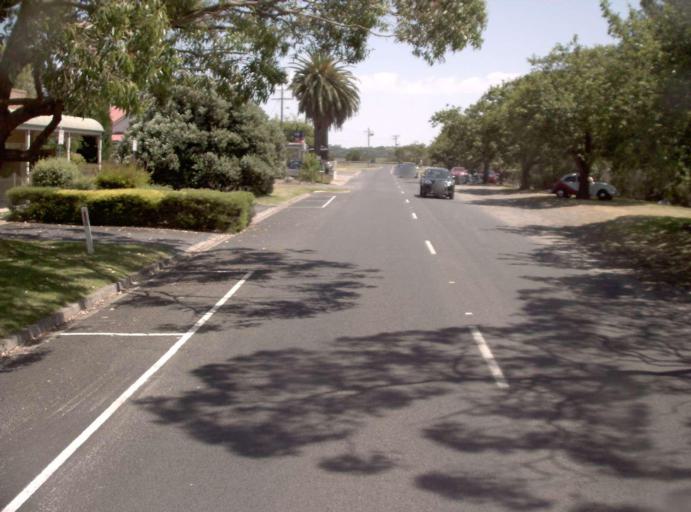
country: AU
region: Victoria
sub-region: Bass Coast
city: North Wonthaggi
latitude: -38.6981
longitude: 145.8663
